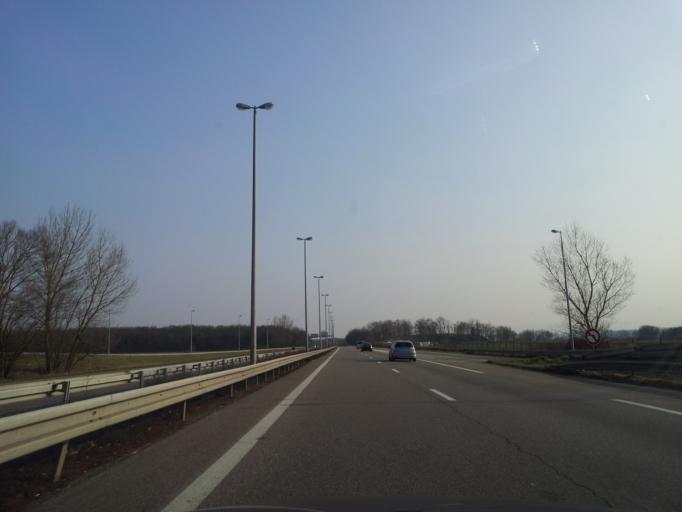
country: FR
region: Alsace
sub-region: Departement du Haut-Rhin
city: Bartenheim
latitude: 47.6354
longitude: 7.5010
